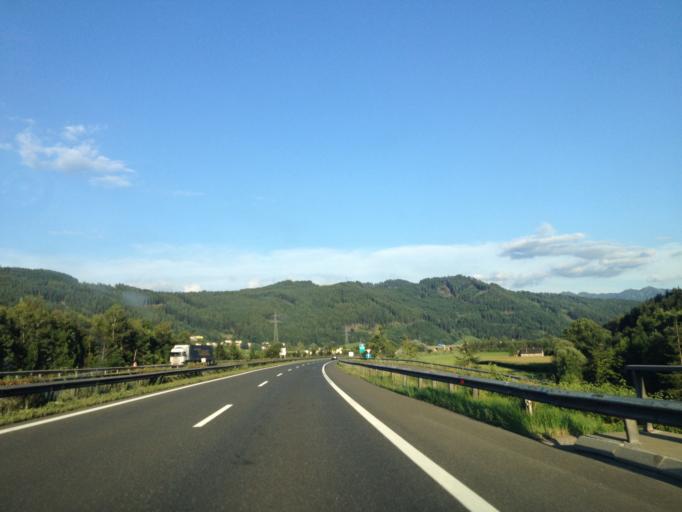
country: AT
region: Styria
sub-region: Politischer Bezirk Leoben
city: Traboch
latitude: 47.3729
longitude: 14.9818
